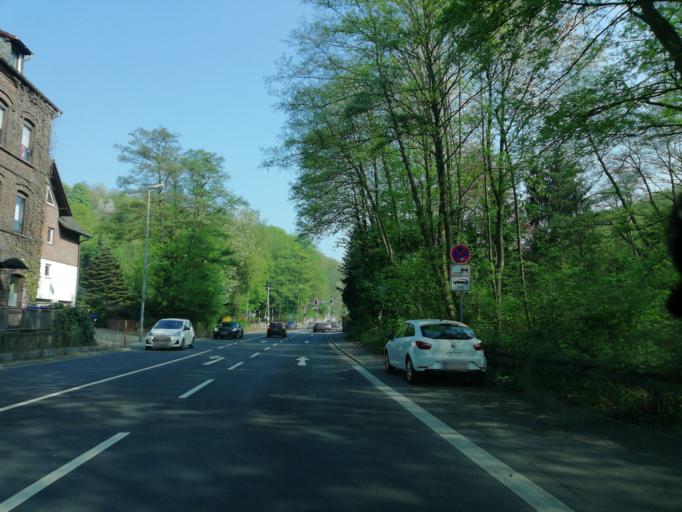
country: DE
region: North Rhine-Westphalia
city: Herdecke
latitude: 51.4115
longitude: 7.4314
